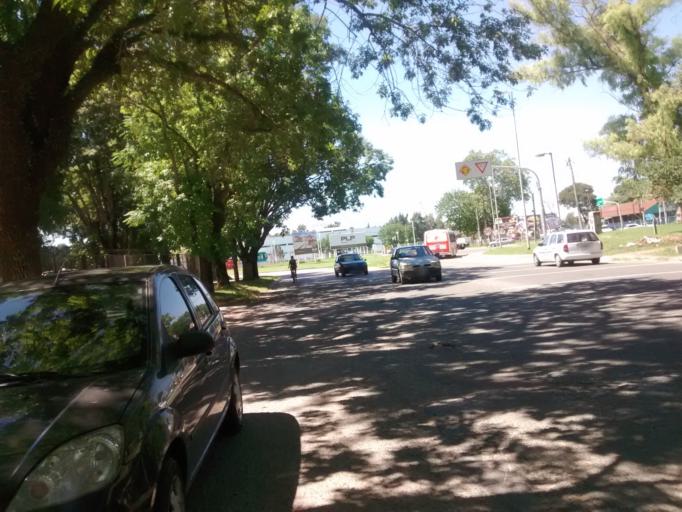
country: AR
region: Buenos Aires
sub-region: Partido de La Plata
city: La Plata
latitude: -34.9030
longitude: -57.9345
